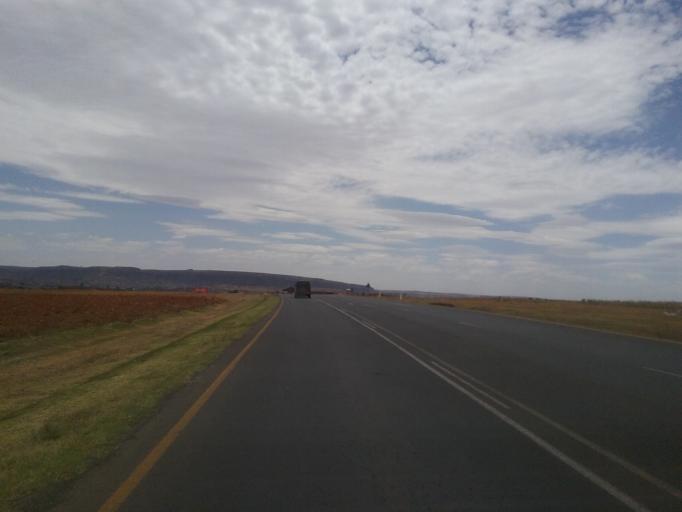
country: LS
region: Maseru
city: Maseru
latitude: -29.4291
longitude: 27.5611
